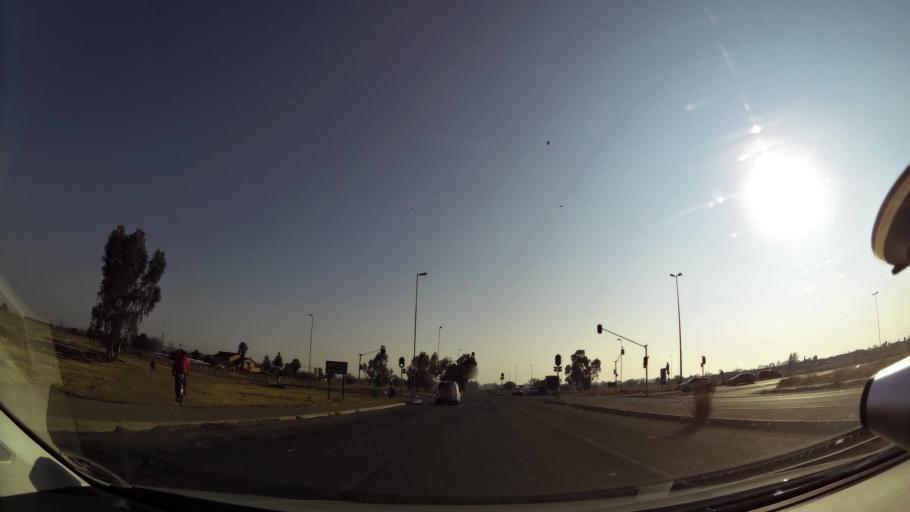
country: ZA
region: Orange Free State
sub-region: Mangaung Metropolitan Municipality
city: Bloemfontein
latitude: -29.1476
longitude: 26.2656
